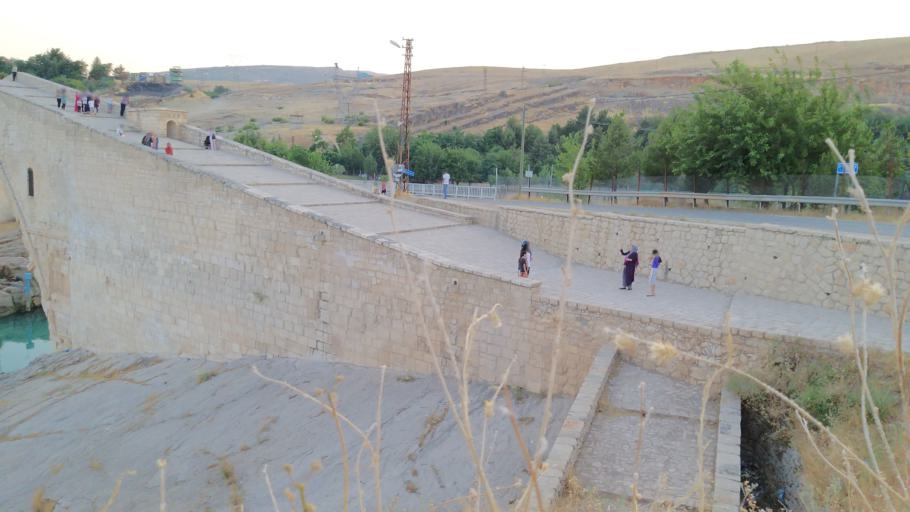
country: TR
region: Diyarbakir
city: Malabadi
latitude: 38.1542
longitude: 41.2045
